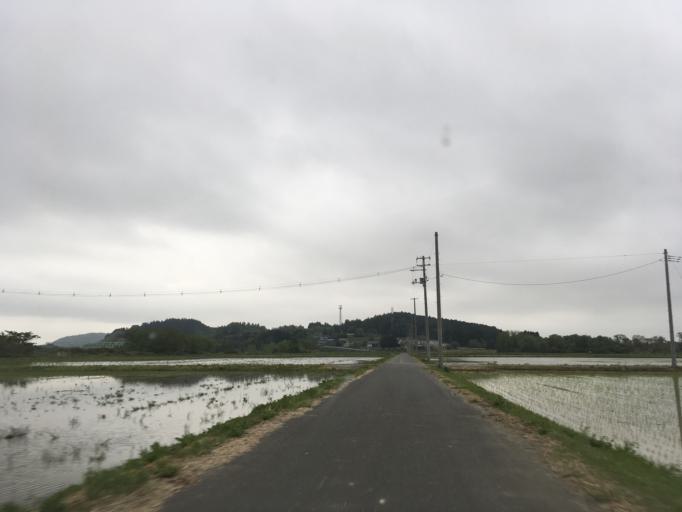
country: JP
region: Miyagi
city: Wakuya
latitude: 38.7147
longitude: 141.2883
